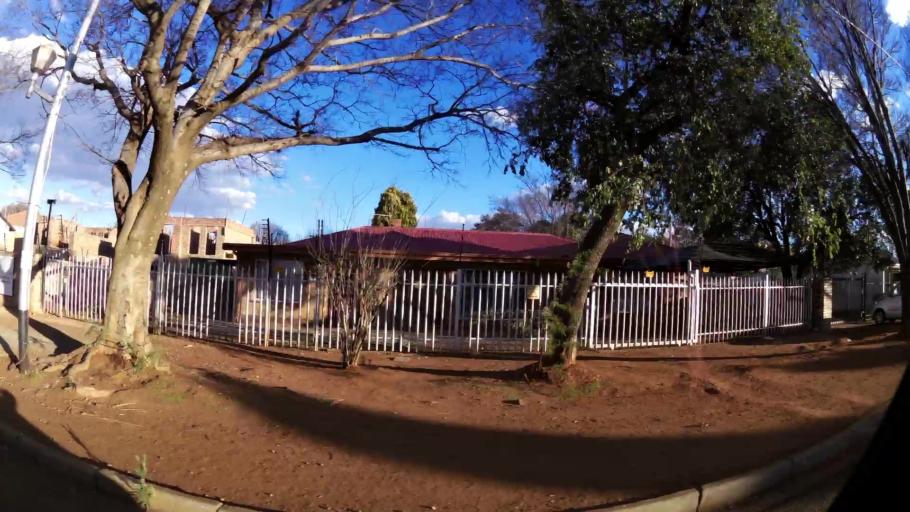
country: ZA
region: North-West
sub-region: Dr Kenneth Kaunda District Municipality
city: Potchefstroom
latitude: -26.6955
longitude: 27.0897
